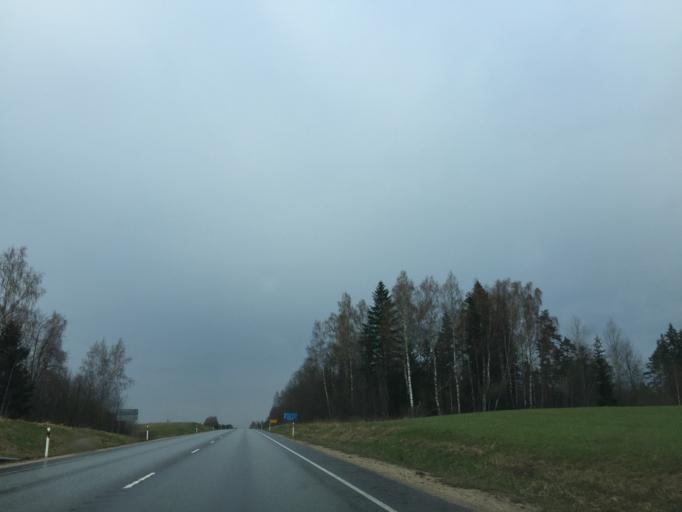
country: EE
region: Tartu
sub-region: UElenurme vald
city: Ulenurme
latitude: 58.1773
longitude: 26.6917
